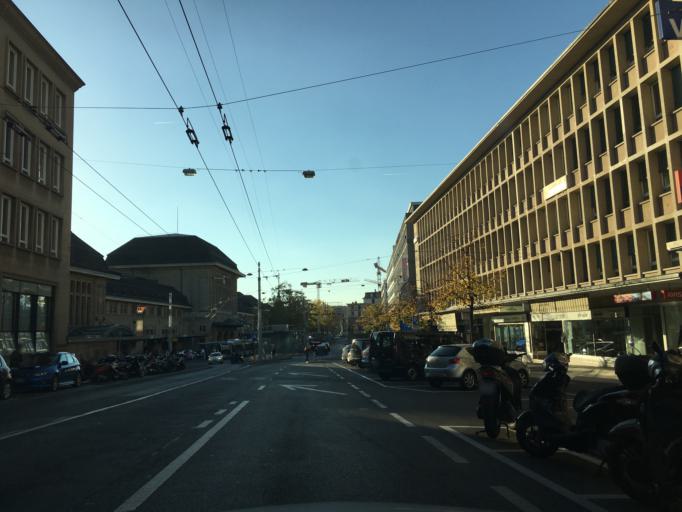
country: CH
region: Vaud
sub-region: Lausanne District
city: Lausanne
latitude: 46.5172
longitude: 6.6315
